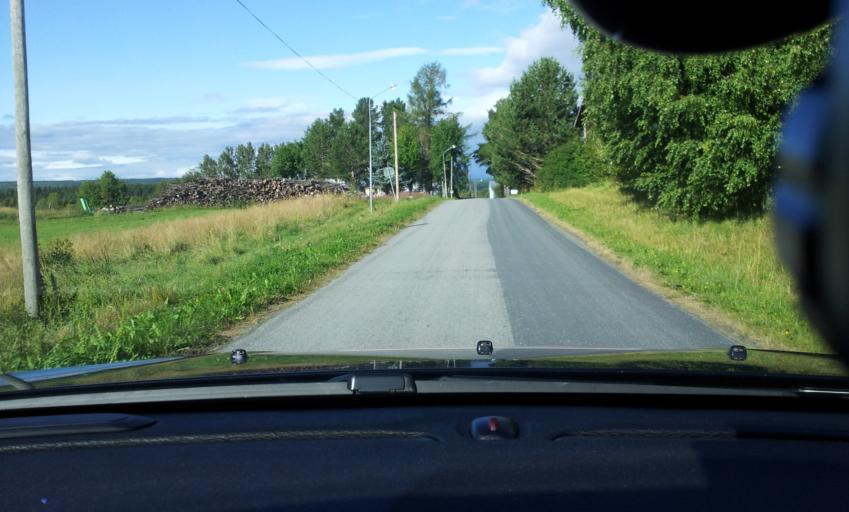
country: SE
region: Jaemtland
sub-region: Krokoms Kommun
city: Valla
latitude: 63.2637
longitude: 13.8395
